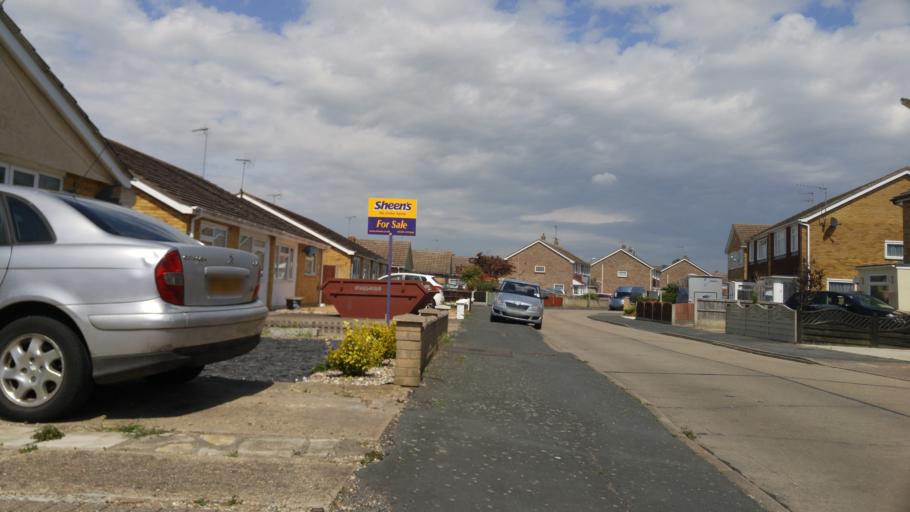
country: GB
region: England
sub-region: Essex
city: Little Clacton
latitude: 51.8136
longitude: 1.1617
